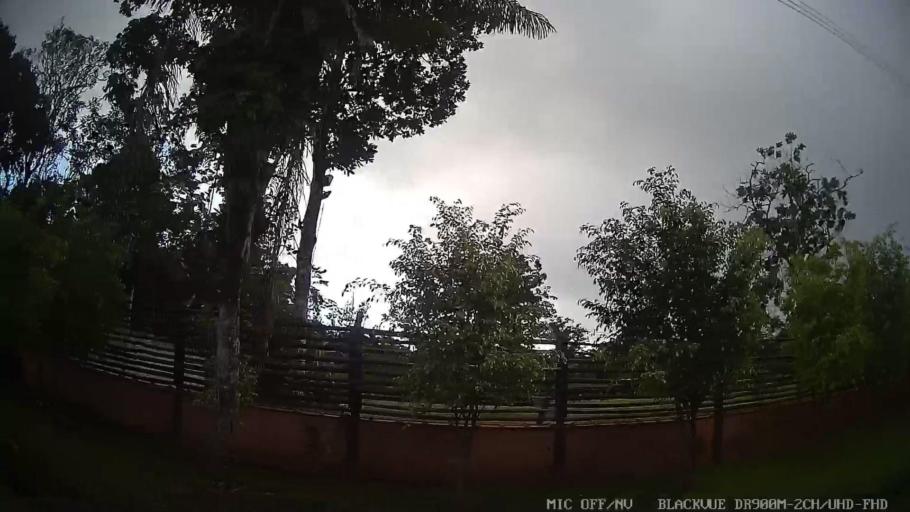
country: BR
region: Sao Paulo
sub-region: Peruibe
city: Peruibe
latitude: -24.2182
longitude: -46.9249
